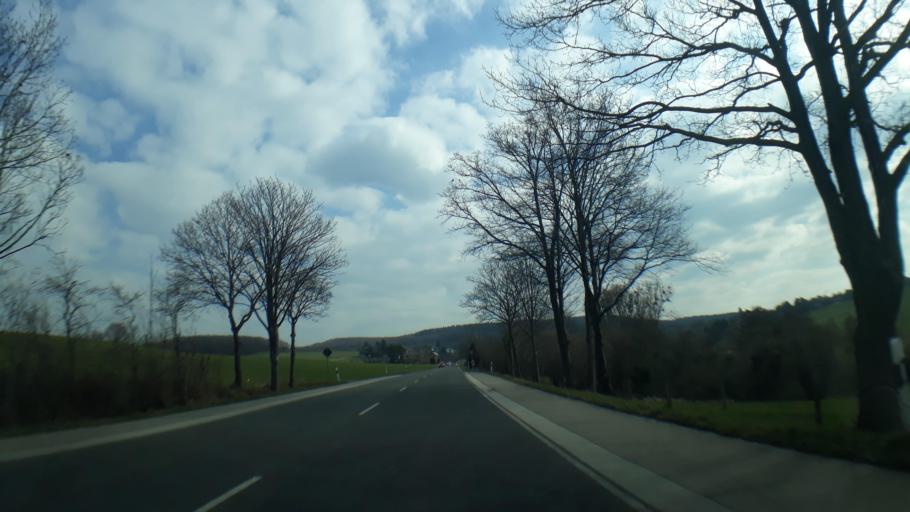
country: DE
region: North Rhine-Westphalia
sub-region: Regierungsbezirk Koln
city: Rheinbach
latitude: 50.6000
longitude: 6.8861
